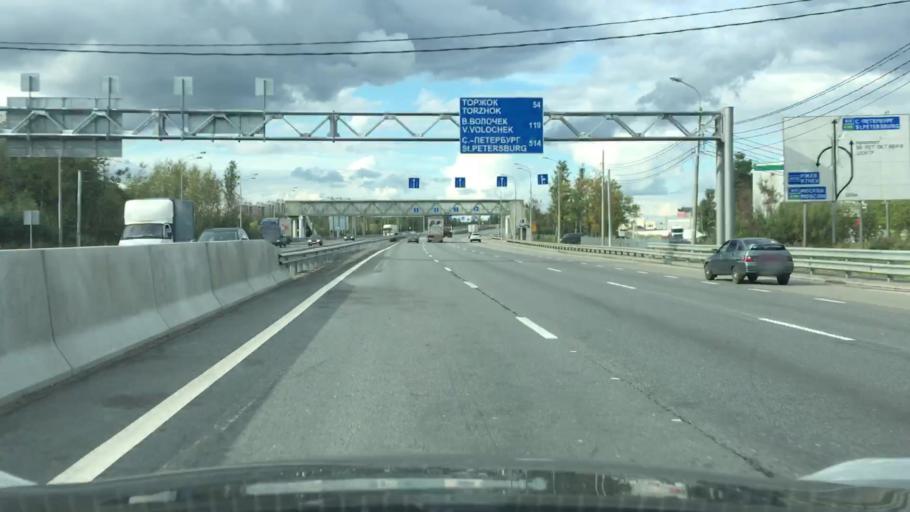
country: RU
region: Tverskaya
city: Tver
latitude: 56.8364
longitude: 35.7965
